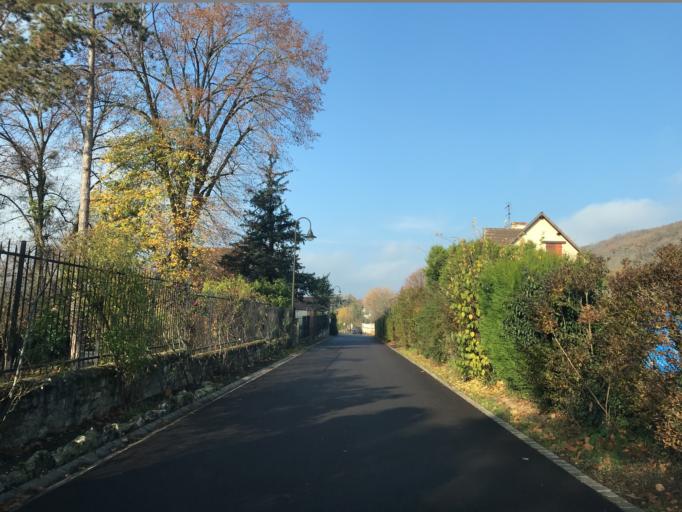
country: FR
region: Ile-de-France
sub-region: Departement des Yvelines
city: Limetz-Villez
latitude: 49.0806
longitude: 1.5181
